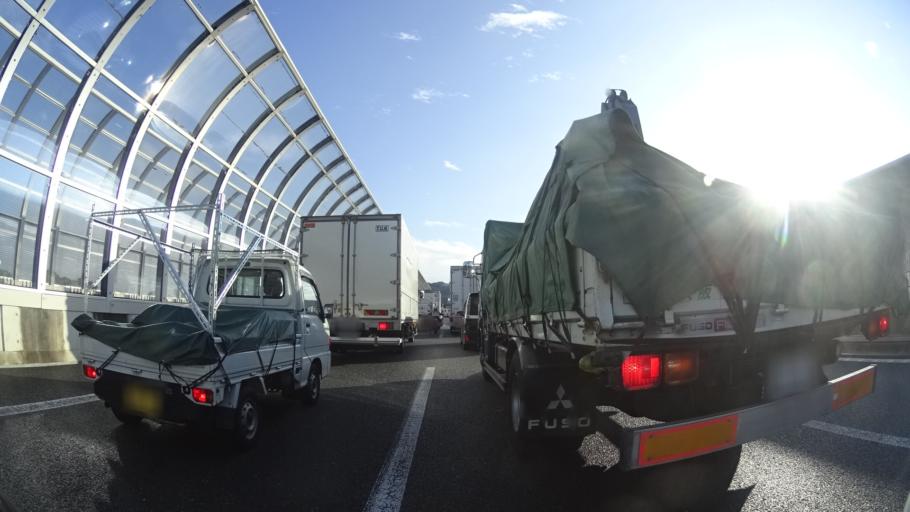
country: JP
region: Osaka
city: Hirakata
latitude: 34.7845
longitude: 135.6836
